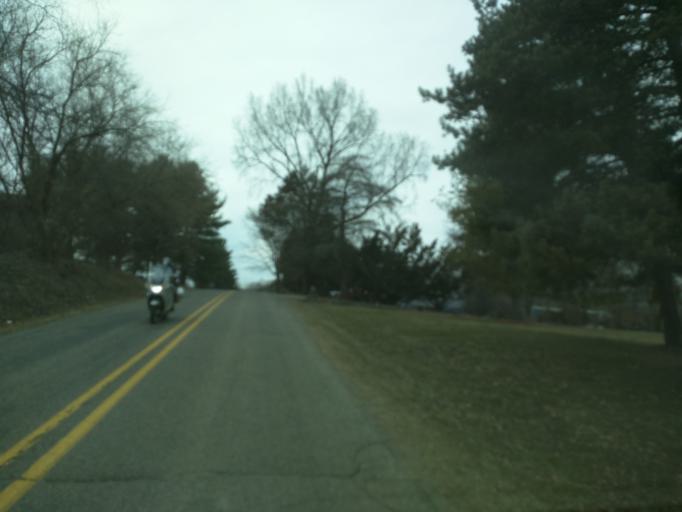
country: US
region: Michigan
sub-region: Ingham County
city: Okemos
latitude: 42.6719
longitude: -84.3995
